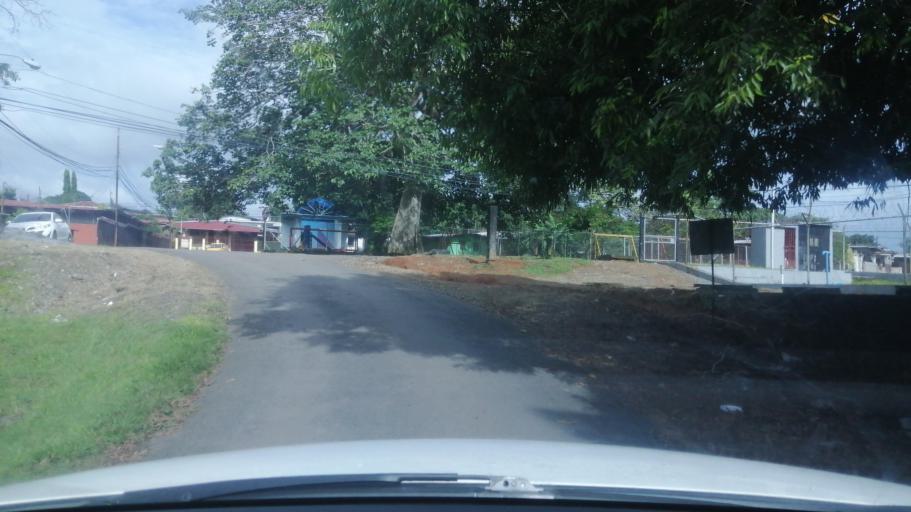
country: PA
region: Chiriqui
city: David
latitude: 8.4107
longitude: -82.4356
